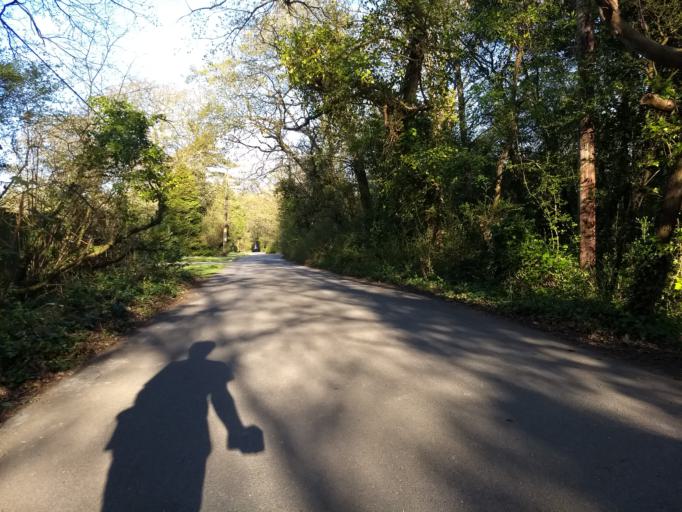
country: GB
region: England
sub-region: Isle of Wight
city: Ryde
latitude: 50.7302
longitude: -1.1939
